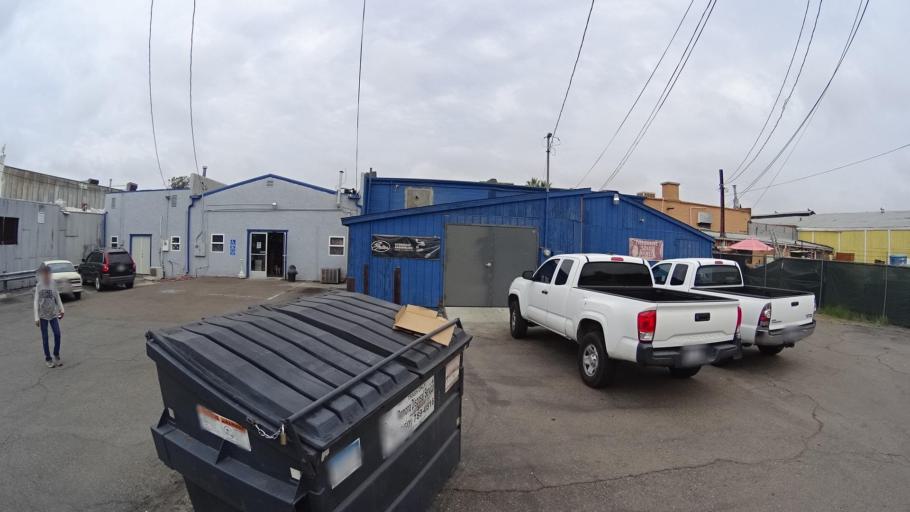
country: US
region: California
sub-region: San Diego County
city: Ramona
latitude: 33.0436
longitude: -116.8645
